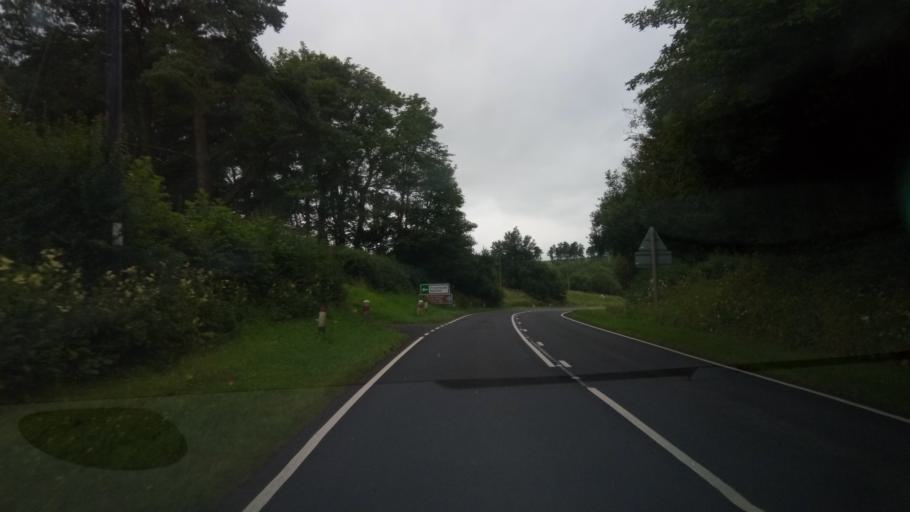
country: GB
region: Scotland
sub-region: The Scottish Borders
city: Hawick
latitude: 55.3616
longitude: -2.8915
